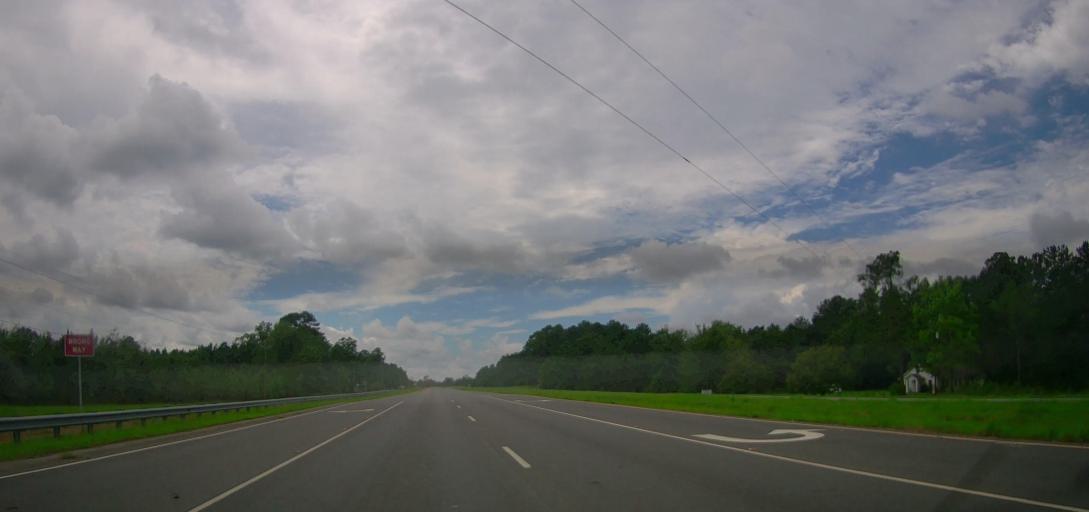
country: US
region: Georgia
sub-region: Telfair County
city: Helena
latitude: 32.1038
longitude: -82.9996
